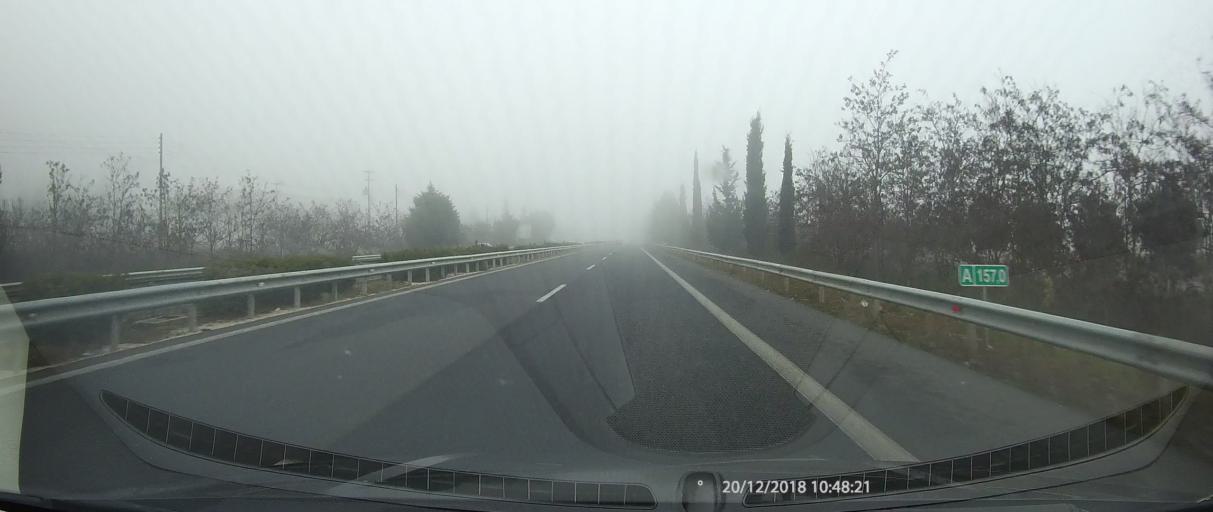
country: GR
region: Peloponnese
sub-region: Nomos Arkadias
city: Tripoli
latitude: 37.5145
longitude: 22.4051
